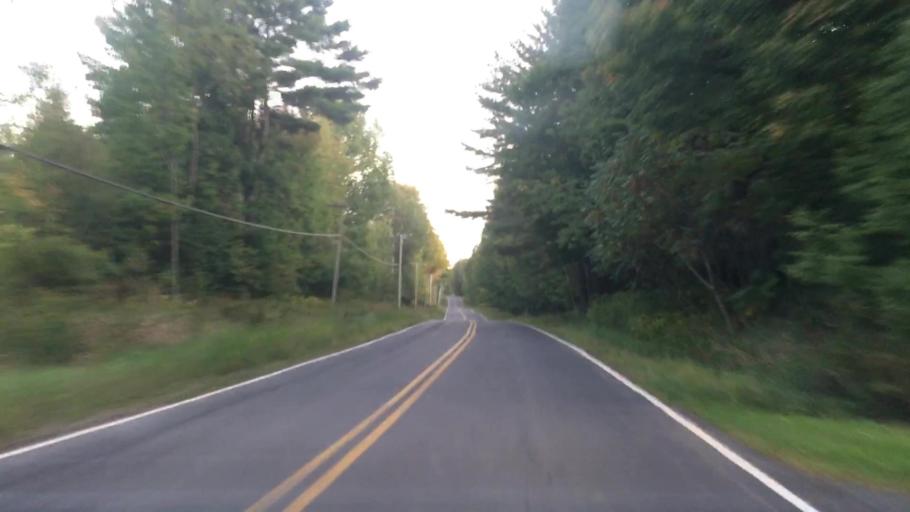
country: US
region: Maine
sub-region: Somerset County
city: Cornville
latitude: 44.8621
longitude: -69.6836
